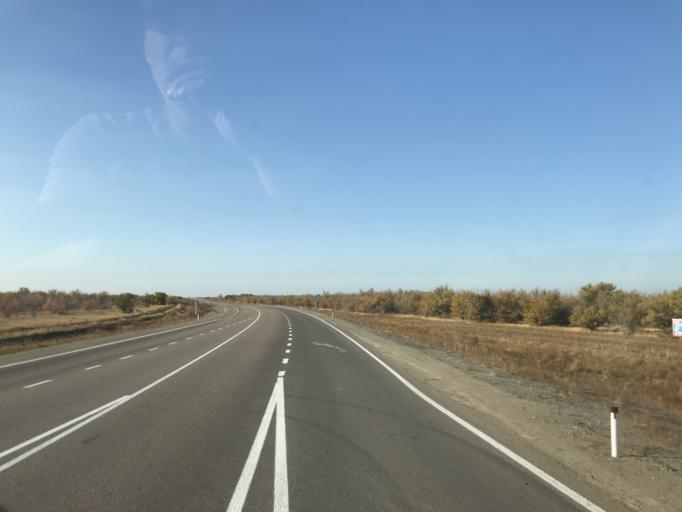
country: KZ
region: Pavlodar
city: Koktobe
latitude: 51.7288
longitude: 77.5591
